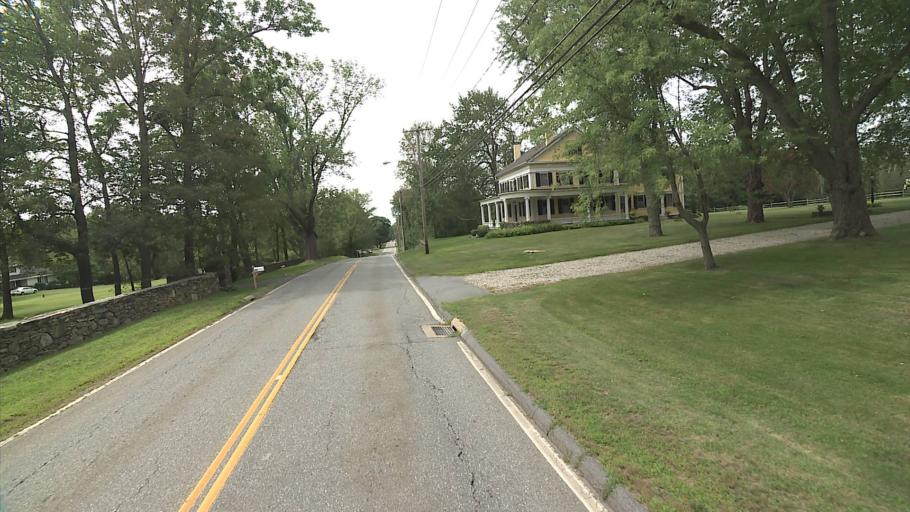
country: US
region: Connecticut
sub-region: Windham County
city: Thompson
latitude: 41.9560
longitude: -71.8646
